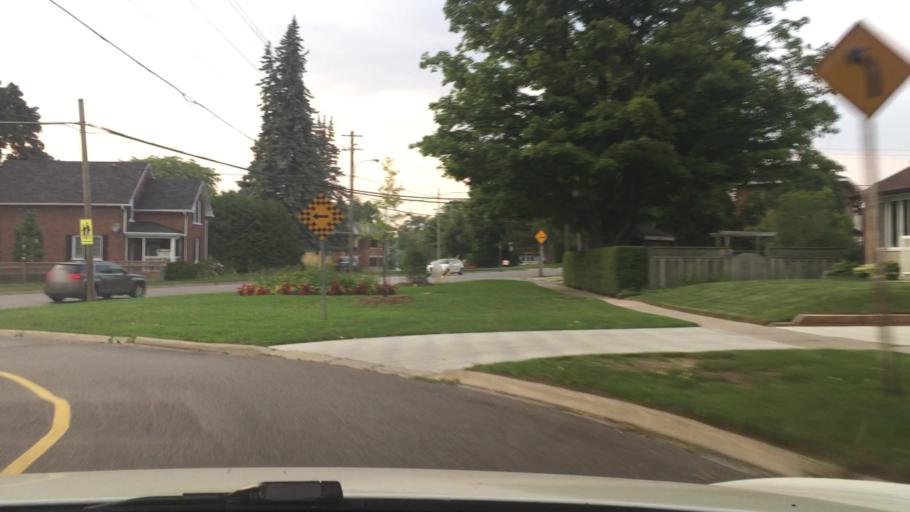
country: CA
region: Ontario
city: Cobourg
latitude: 43.9611
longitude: -78.2910
